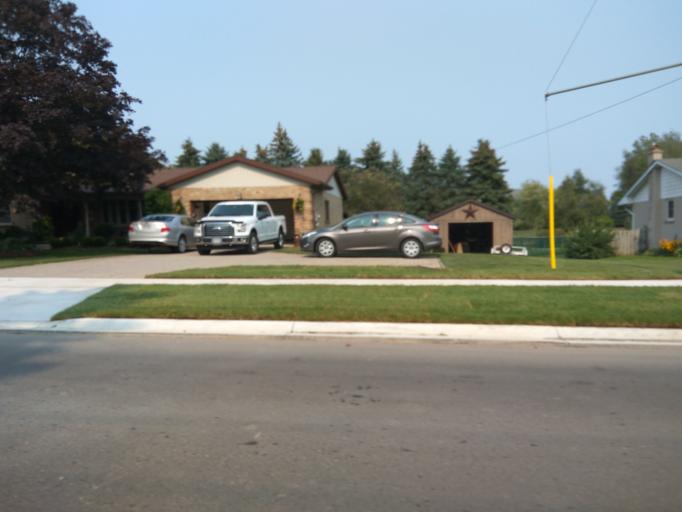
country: CA
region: Ontario
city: Kitchener
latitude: 43.4109
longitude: -80.6023
